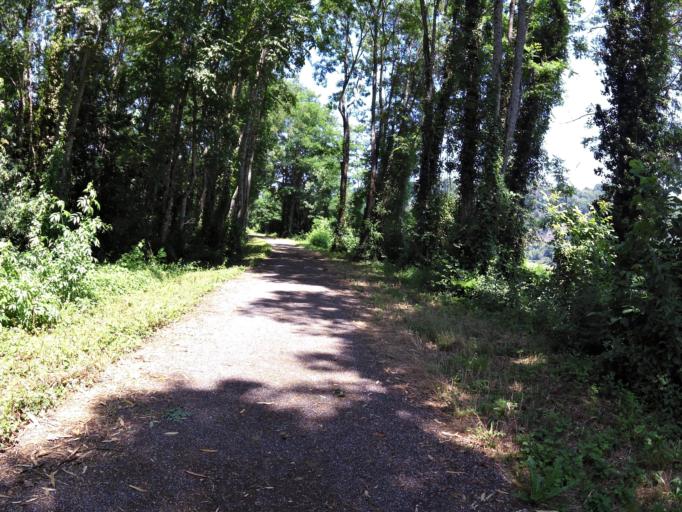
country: FR
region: Aquitaine
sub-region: Departement des Pyrenees-Atlantiques
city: Sauveterre-de-Bearn
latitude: 43.4447
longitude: -0.9936
